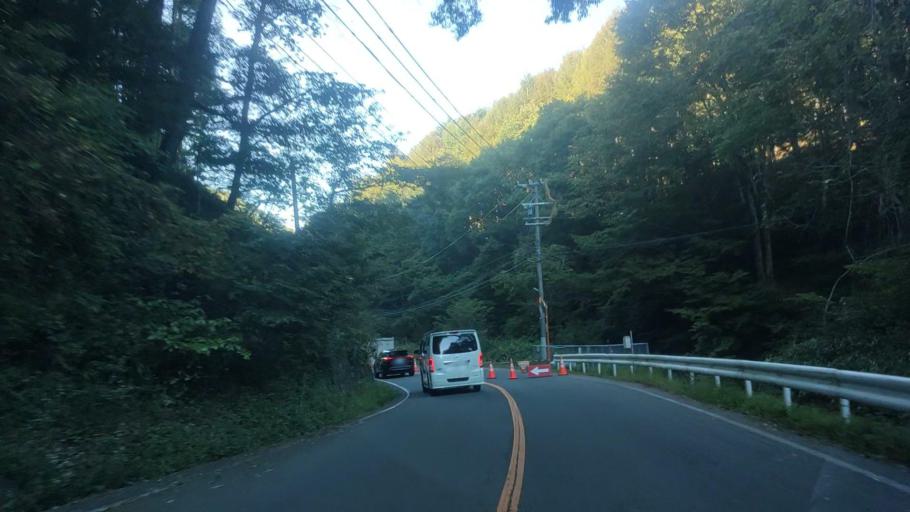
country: JP
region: Nagano
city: Kamimaruko
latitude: 36.2405
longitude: 138.3050
